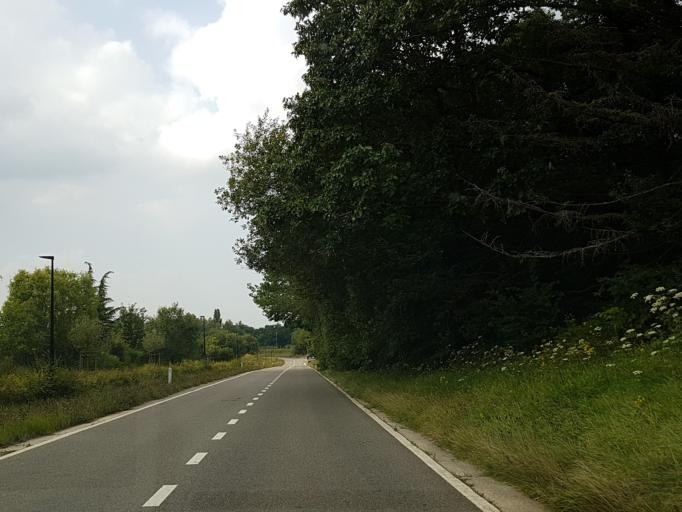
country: BE
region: Flanders
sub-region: Provincie Vlaams-Brabant
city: Wezembeek-Oppem
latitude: 50.8669
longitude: 4.5098
